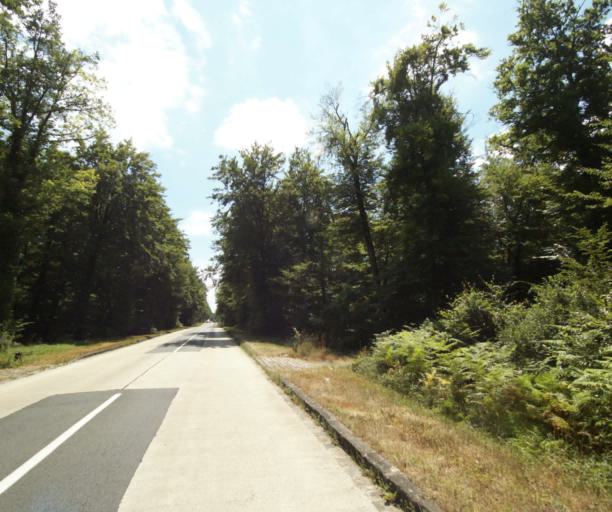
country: FR
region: Ile-de-France
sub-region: Departement de Seine-et-Marne
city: Bois-le-Roi
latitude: 48.4487
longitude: 2.7123
